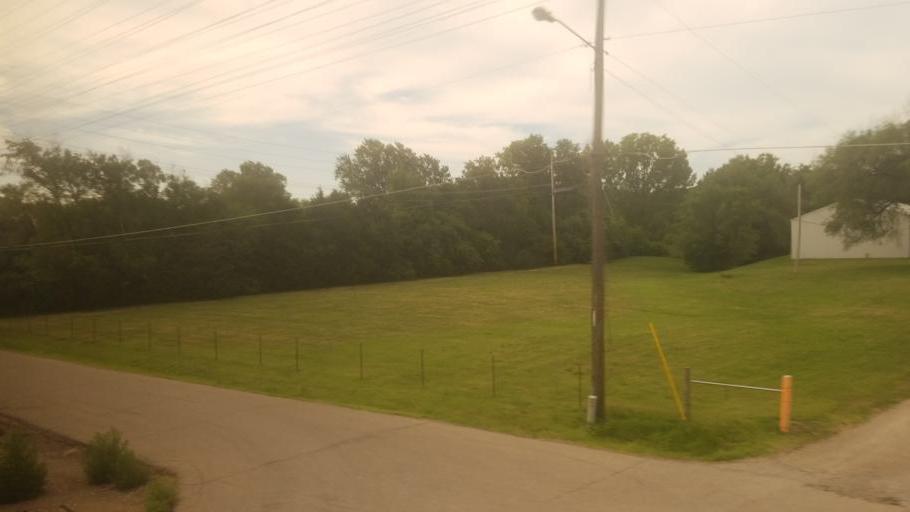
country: US
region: Kansas
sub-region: Shawnee County
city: Topeka
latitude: 39.0554
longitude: -95.6274
